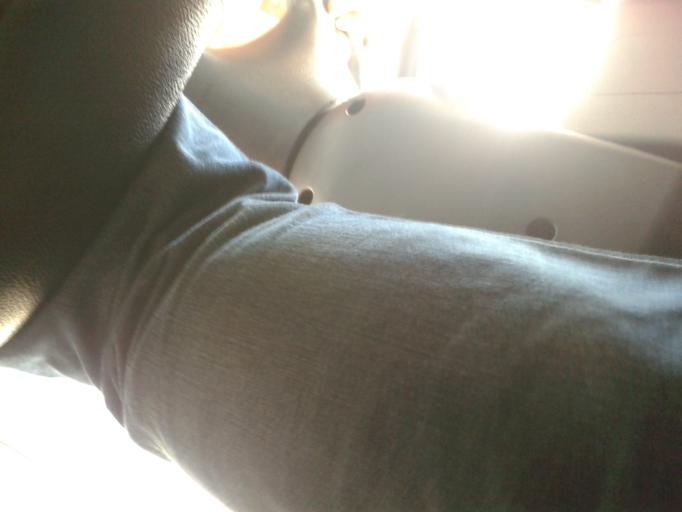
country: BR
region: Minas Gerais
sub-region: Ituiutaba
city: Ituiutaba
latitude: -19.0775
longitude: -49.7545
